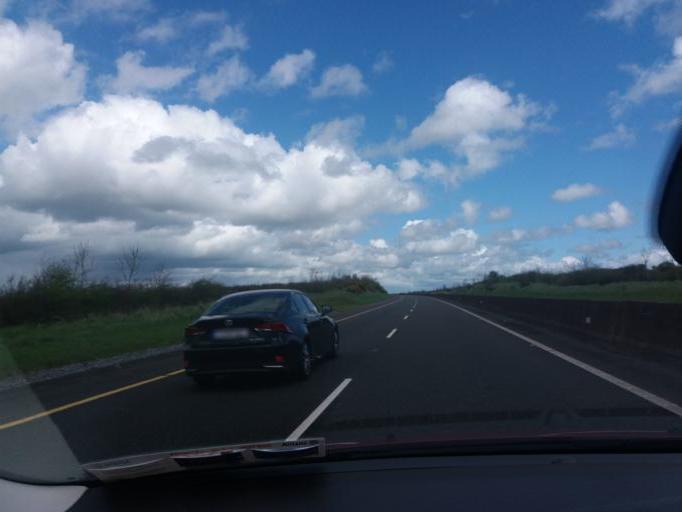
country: IE
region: Leinster
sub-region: Laois
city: Rathdowney
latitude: 52.7671
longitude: -7.5487
